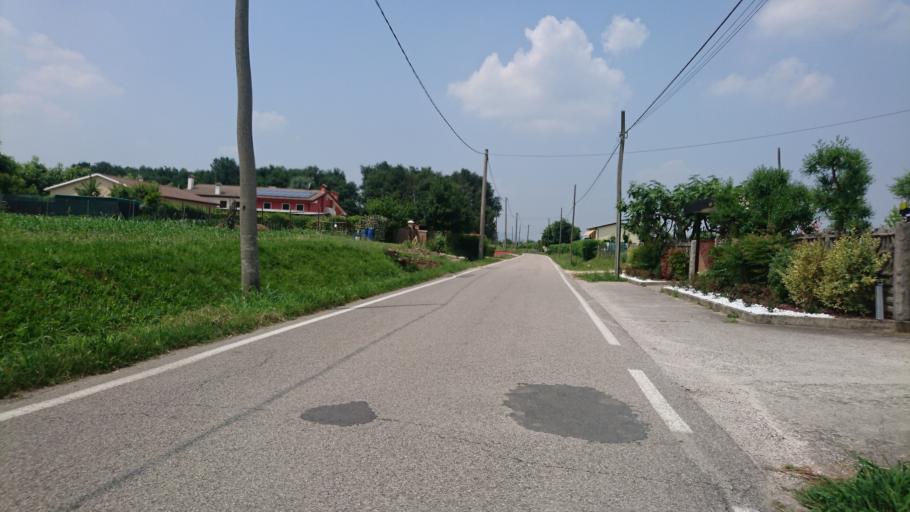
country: IT
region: Veneto
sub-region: Provincia di Padova
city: Cartura
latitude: 45.2638
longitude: 11.8780
